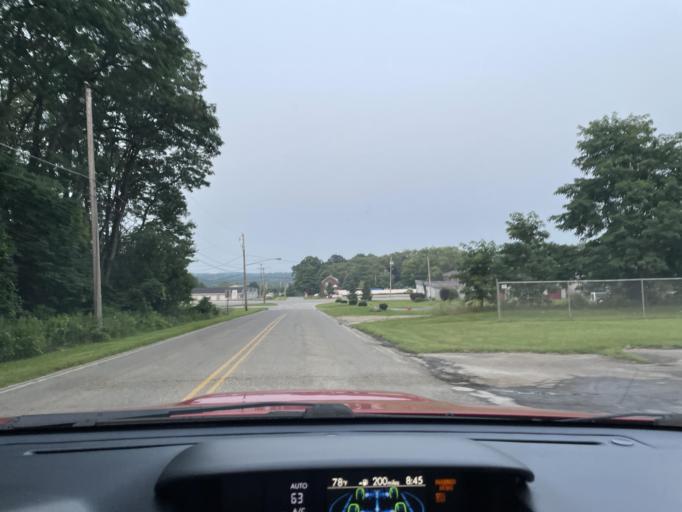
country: US
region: Ohio
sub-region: Trumbull County
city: McDonald
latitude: 41.1687
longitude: -80.7262
